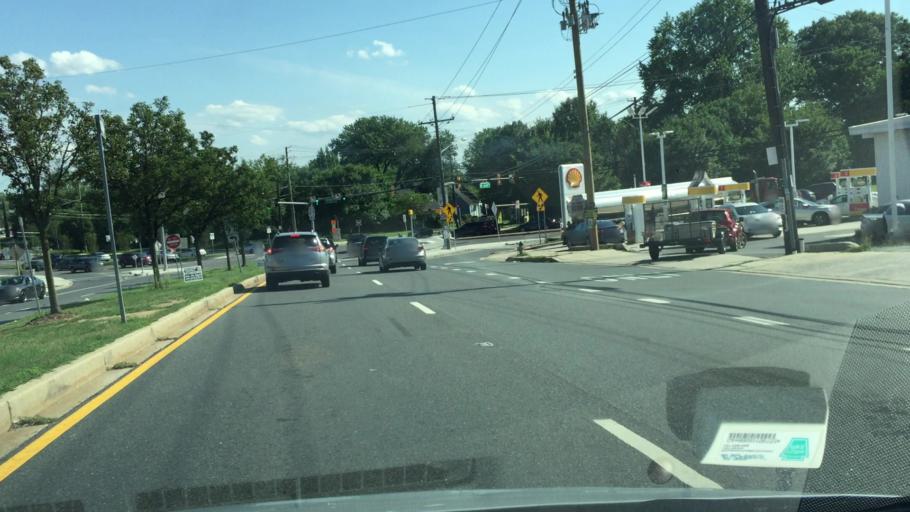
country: US
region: Maryland
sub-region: Montgomery County
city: Glenmont
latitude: 39.0611
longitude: -77.0510
